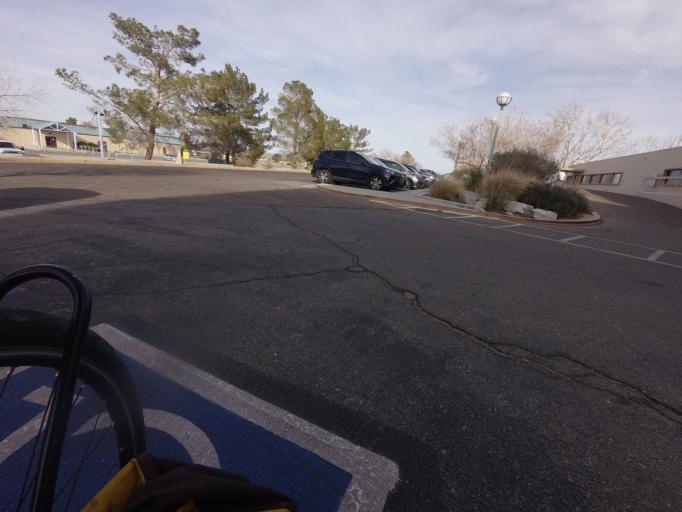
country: US
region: California
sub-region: Kern County
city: Ridgecrest
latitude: 35.6420
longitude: -117.6713
